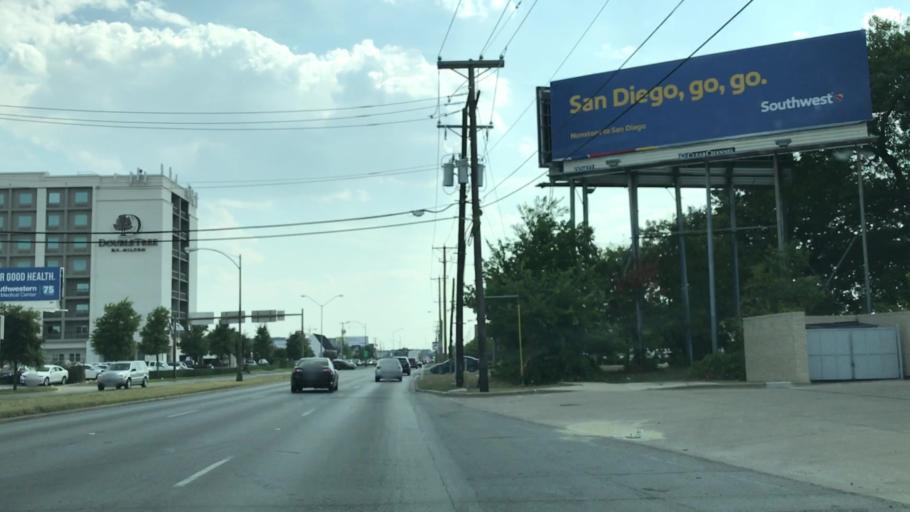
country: US
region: Texas
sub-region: Dallas County
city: University Park
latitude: 32.8355
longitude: -96.8356
